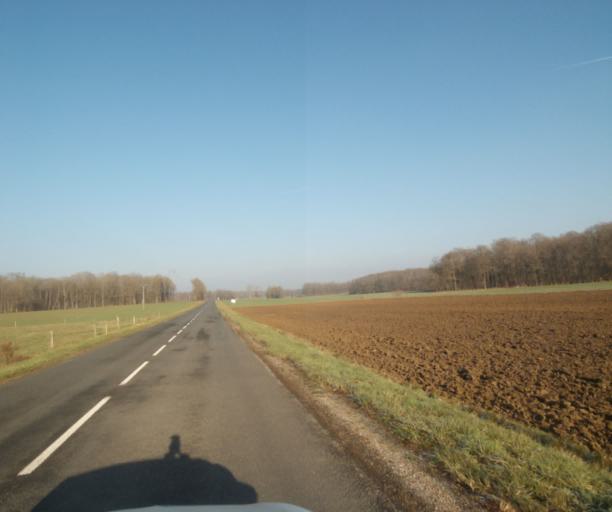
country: FR
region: Champagne-Ardenne
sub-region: Departement de la Haute-Marne
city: Montier-en-Der
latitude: 48.5030
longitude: 4.7498
